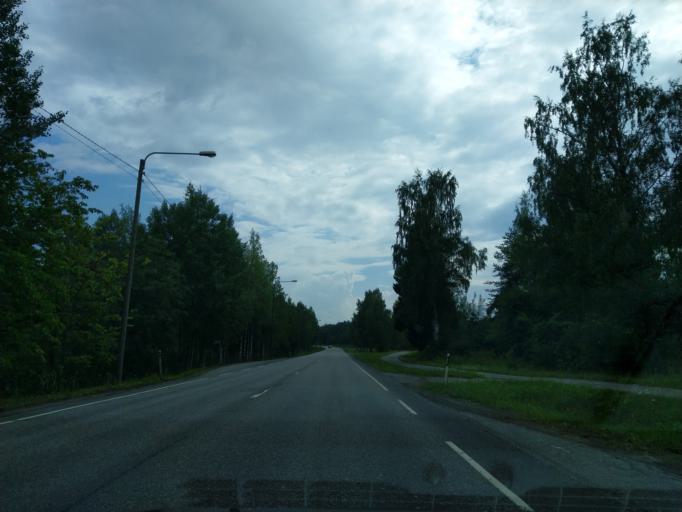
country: FI
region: South Karelia
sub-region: Imatra
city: Parikkala
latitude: 61.5983
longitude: 29.4835
